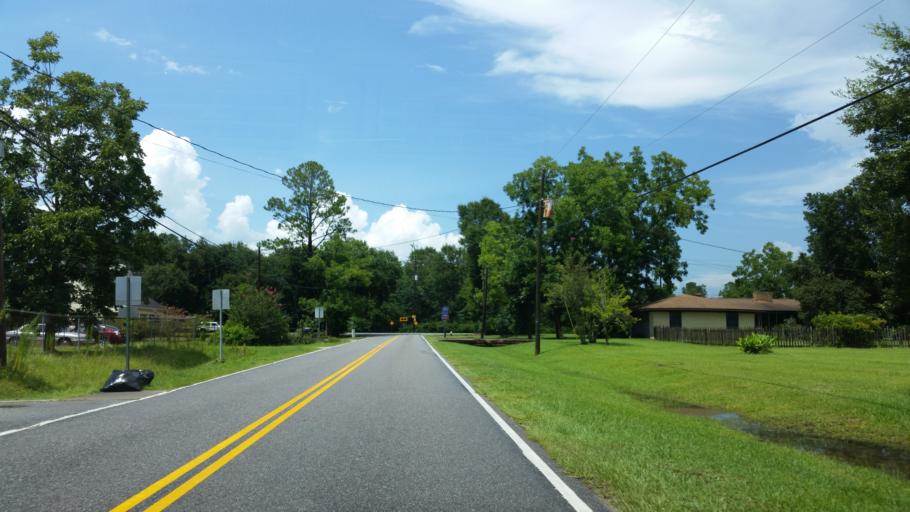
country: US
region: Florida
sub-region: Escambia County
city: Gonzalez
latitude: 30.5619
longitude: -87.2996
